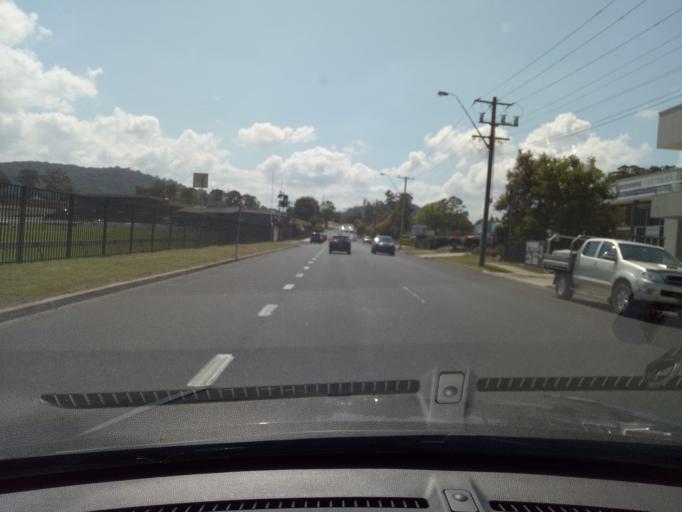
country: AU
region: New South Wales
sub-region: Gosford Shire
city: Gosford
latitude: -33.4239
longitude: 151.3279
